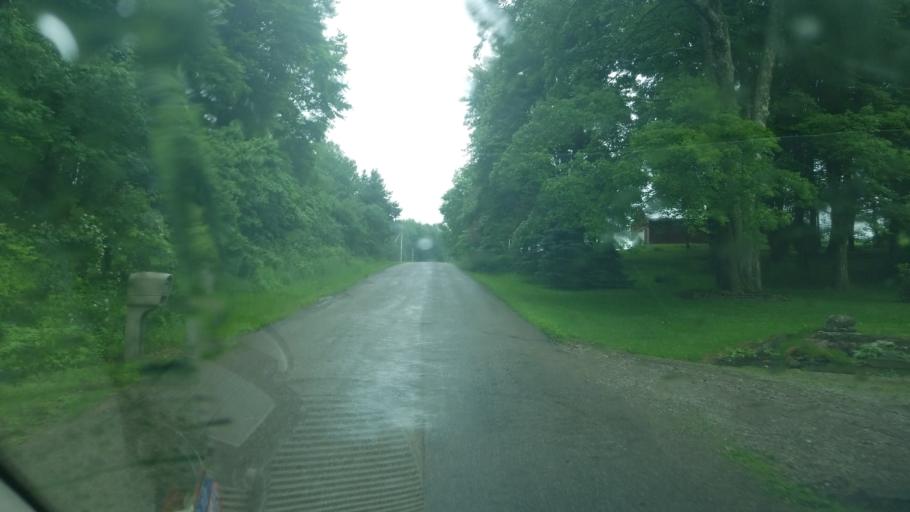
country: US
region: Ohio
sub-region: Sandusky County
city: Bellville
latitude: 40.6372
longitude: -82.4150
